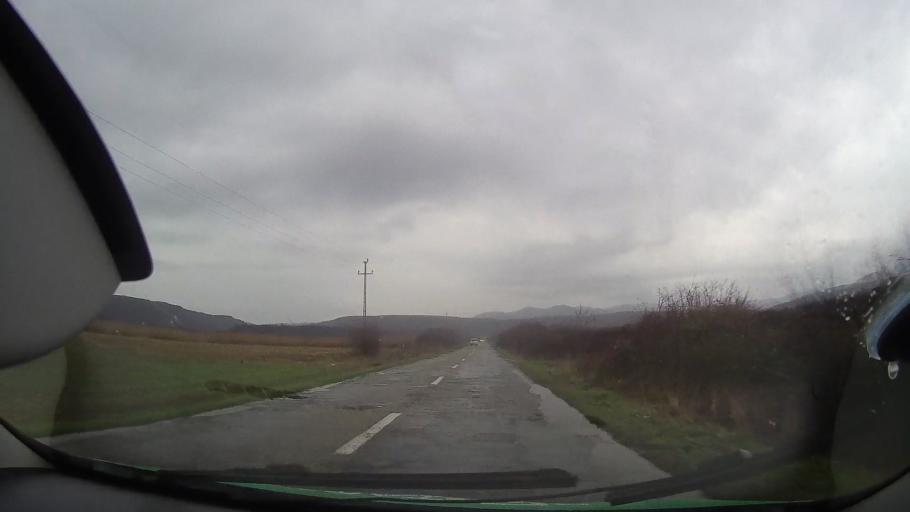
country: RO
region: Bihor
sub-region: Comuna Soimi
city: Soimi
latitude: 46.6916
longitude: 22.1001
